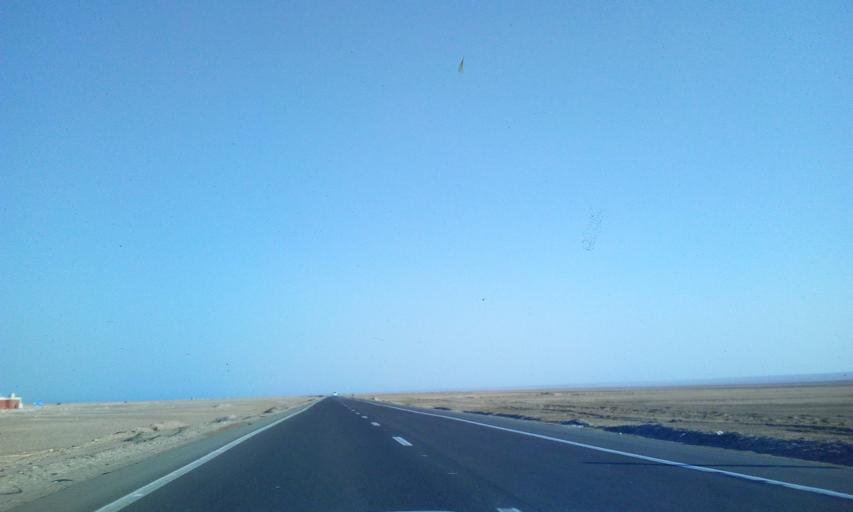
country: EG
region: South Sinai
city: Tor
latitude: 28.6574
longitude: 32.8434
